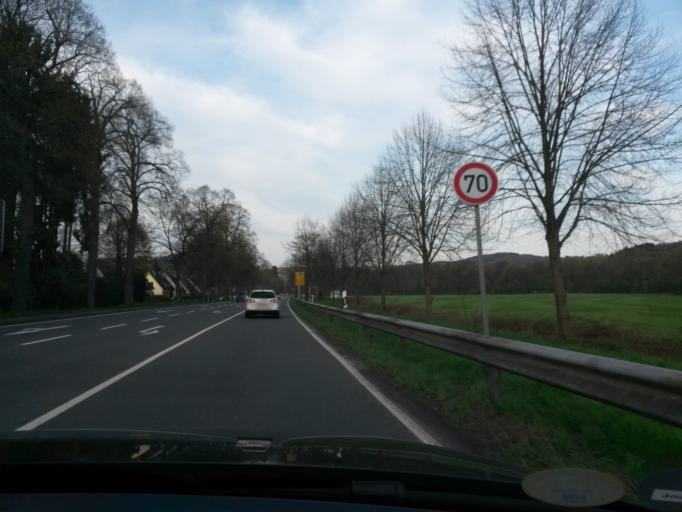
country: DE
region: North Rhine-Westphalia
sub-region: Regierungsbezirk Koln
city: Overath
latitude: 50.8928
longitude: 7.2532
